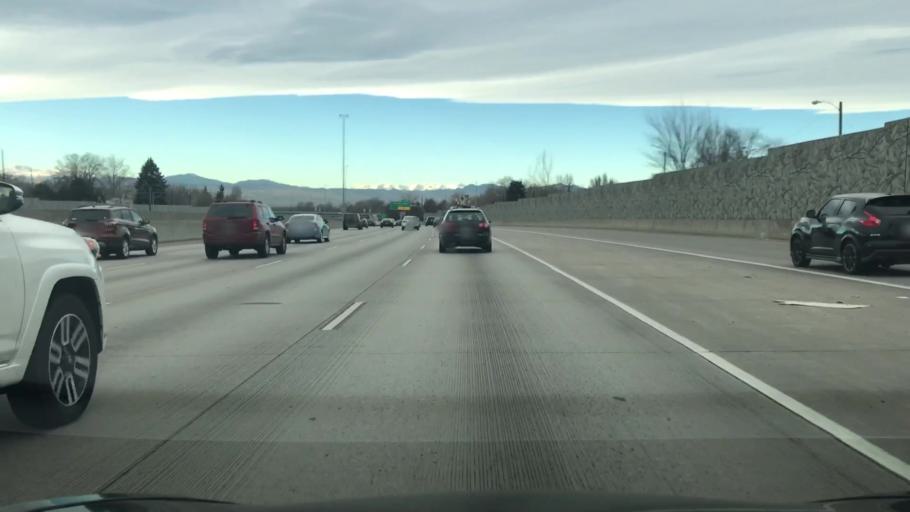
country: US
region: Colorado
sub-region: Arapahoe County
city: Glendale
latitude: 39.6850
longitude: -104.9451
